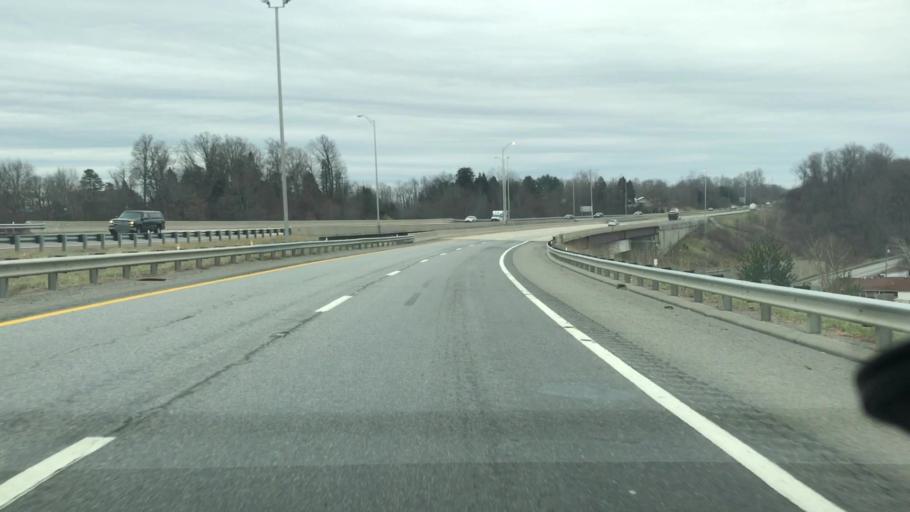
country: US
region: Virginia
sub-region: Montgomery County
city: Merrimac
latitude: 37.1847
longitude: -80.4027
